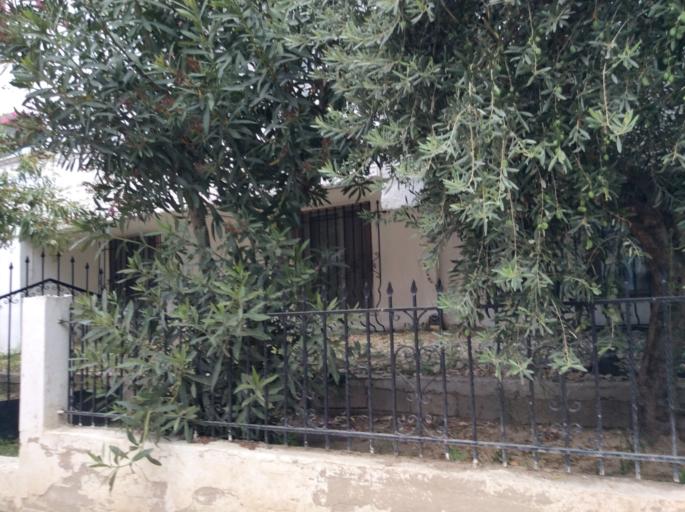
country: GR
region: Central Macedonia
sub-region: Nomos Chalkidikis
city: Sykia
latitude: 39.9886
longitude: 23.8997
